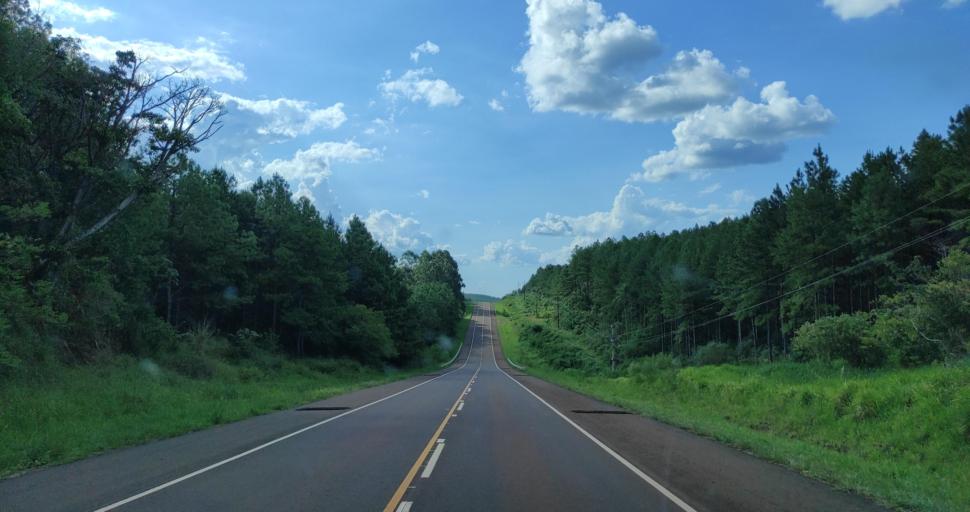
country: AR
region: Misiones
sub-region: Departamento de San Pedro
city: San Pedro
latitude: -26.3651
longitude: -53.9479
